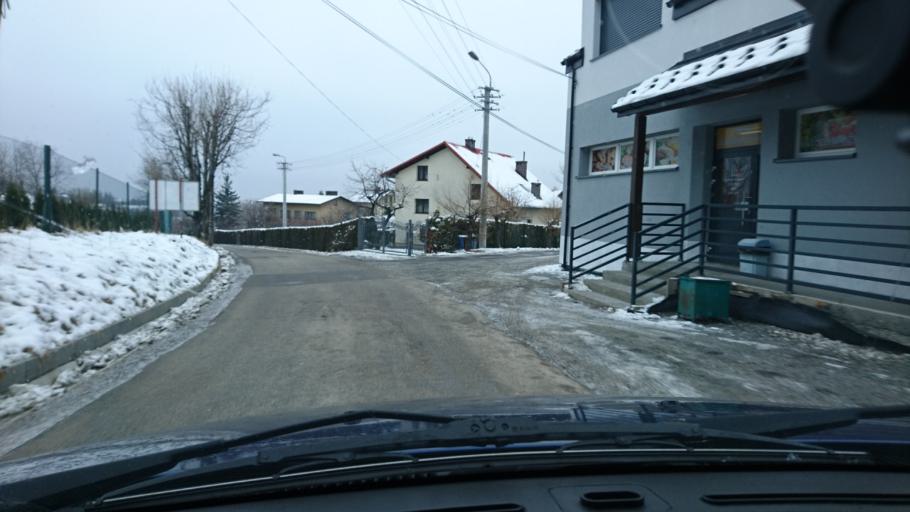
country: PL
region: Silesian Voivodeship
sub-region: Powiat bielski
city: Kozy
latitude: 49.8215
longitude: 19.1198
